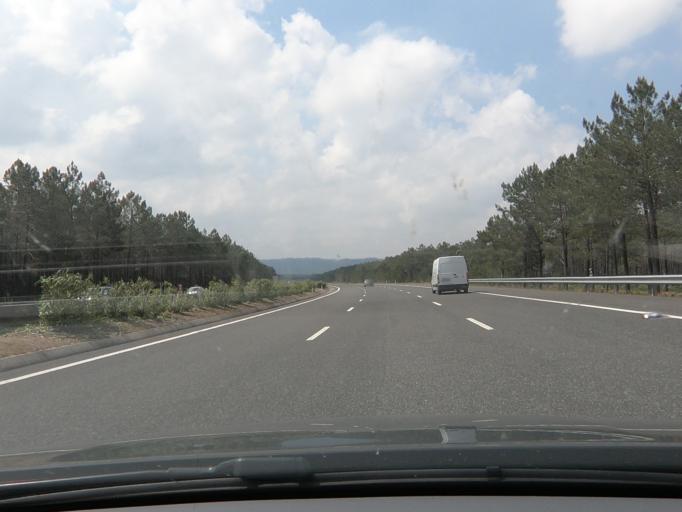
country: PT
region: Leiria
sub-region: Alcobaca
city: Pataias
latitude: 39.6107
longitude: -8.9998
